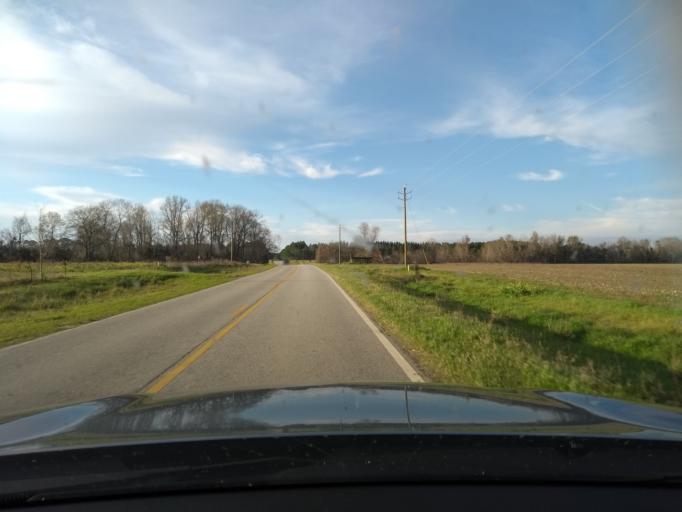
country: US
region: Georgia
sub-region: Bulloch County
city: Brooklet
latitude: 32.3063
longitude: -81.7742
